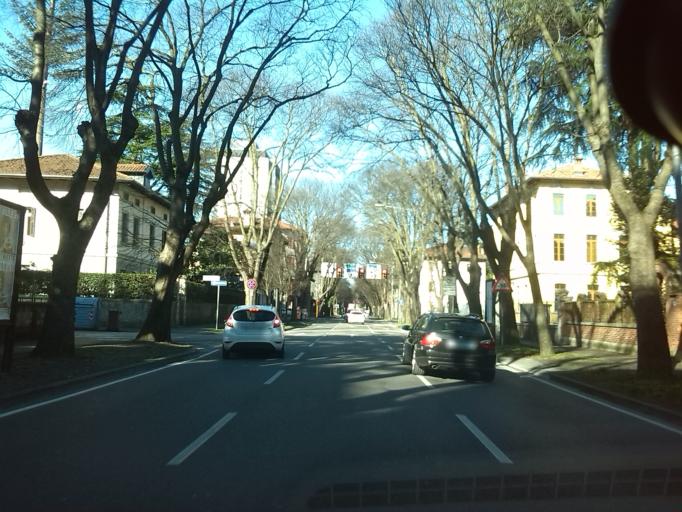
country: IT
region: Friuli Venezia Giulia
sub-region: Provincia di Udine
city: Udine
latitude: 46.0715
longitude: 13.2407
